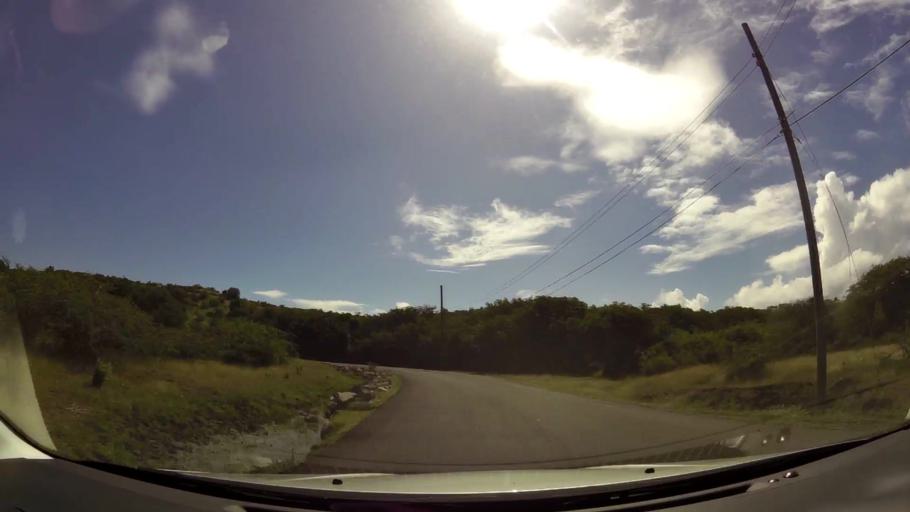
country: AG
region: Saint Paul
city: Falmouth
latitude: 17.0339
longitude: -61.7467
